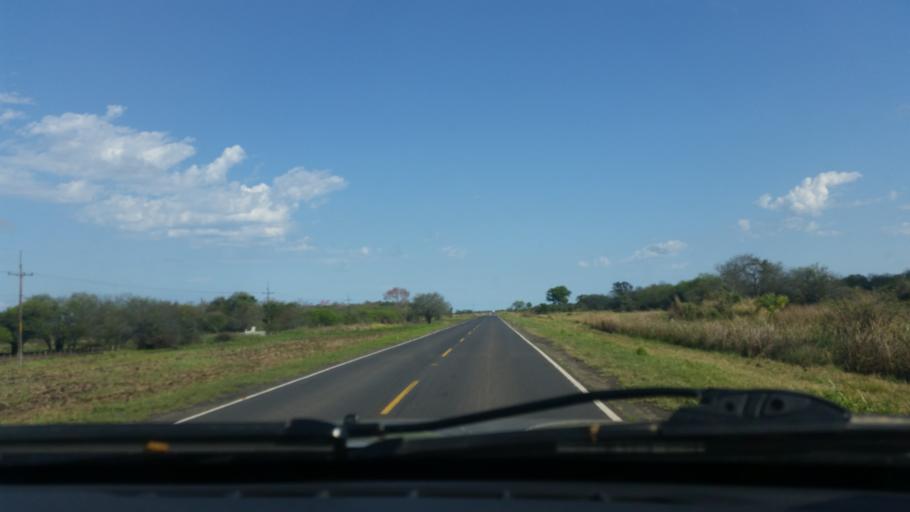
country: PY
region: Presidente Hayes
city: Benjamin Aceval
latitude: -24.8995
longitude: -57.6577
